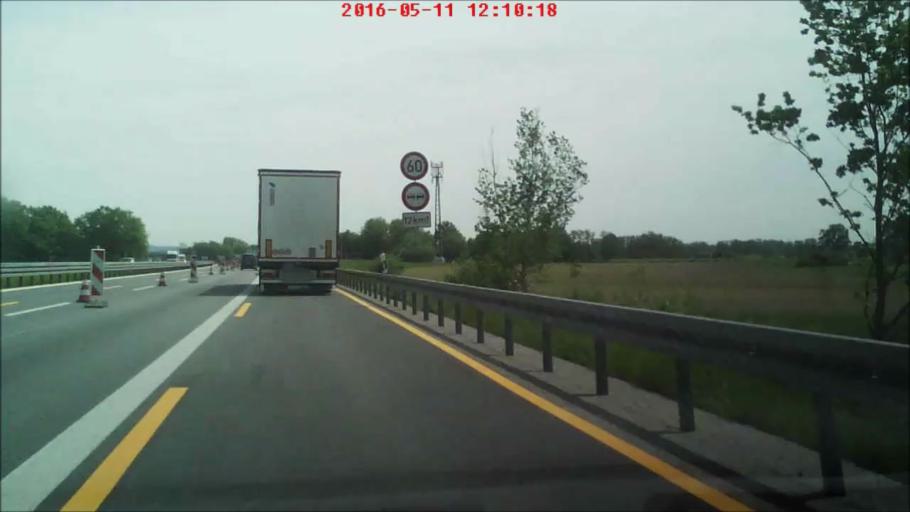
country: DE
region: Bavaria
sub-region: Lower Bavaria
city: Offenberg
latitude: 48.8628
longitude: 12.8504
